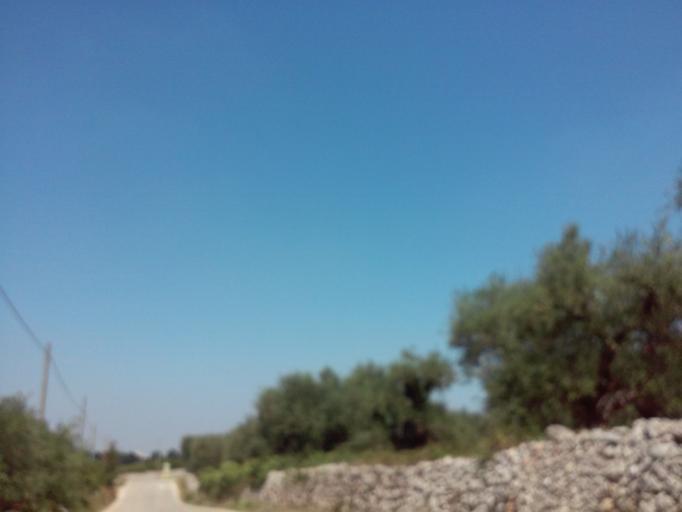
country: IT
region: Apulia
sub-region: Provincia di Bari
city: Alberobello
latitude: 40.7949
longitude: 17.2207
